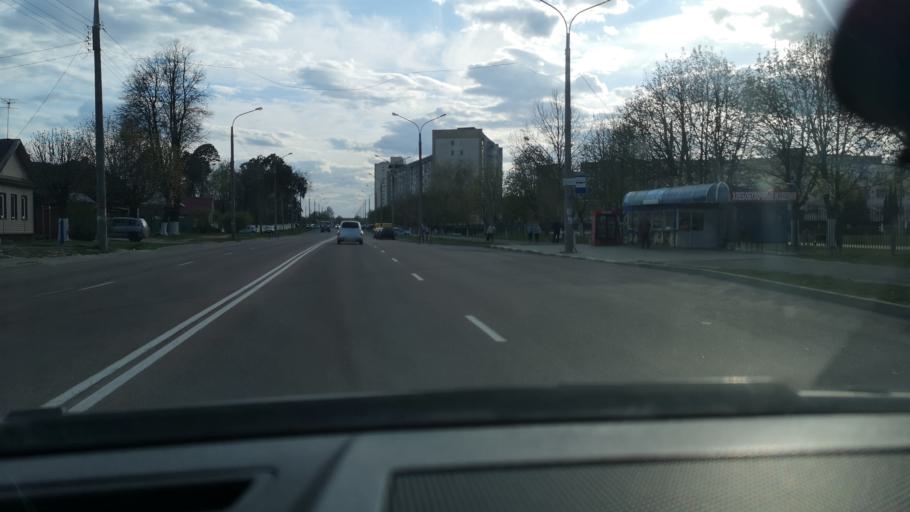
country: BY
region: Gomel
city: Gomel
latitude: 52.4025
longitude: 30.9297
